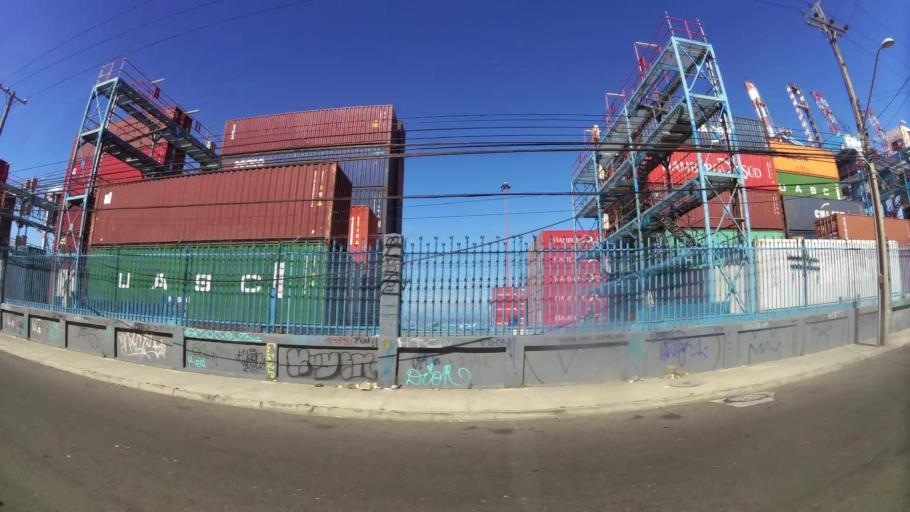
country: CL
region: Valparaiso
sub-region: Provincia de Valparaiso
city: Valparaiso
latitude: -33.0296
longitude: -71.6289
